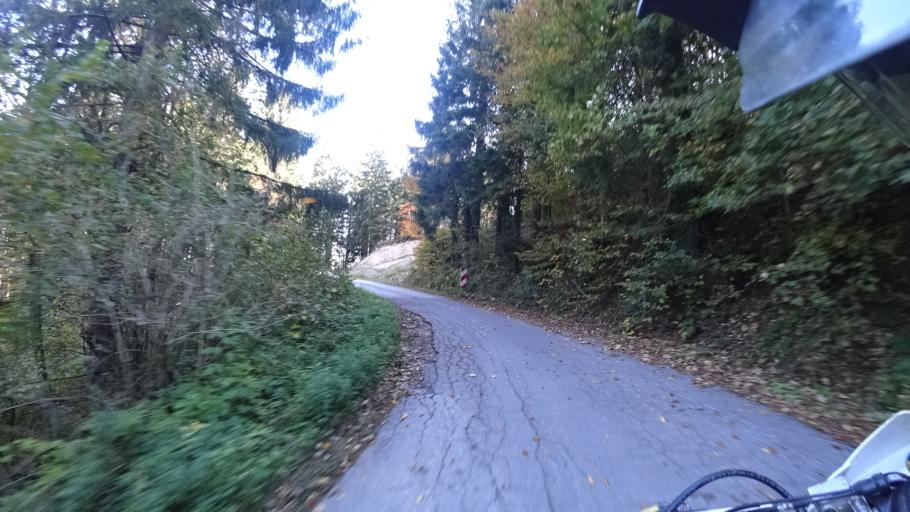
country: HR
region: Karlovacka
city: Plaski
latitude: 44.9874
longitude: 15.4167
